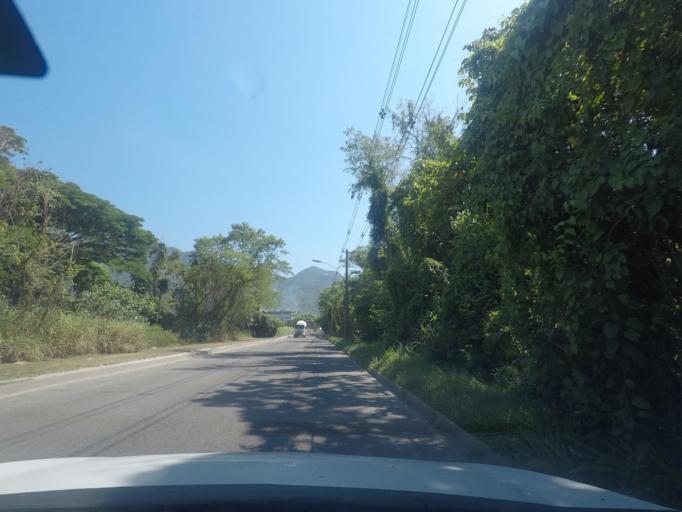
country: BR
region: Rio de Janeiro
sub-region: Nilopolis
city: Nilopolis
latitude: -22.9877
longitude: -43.4538
